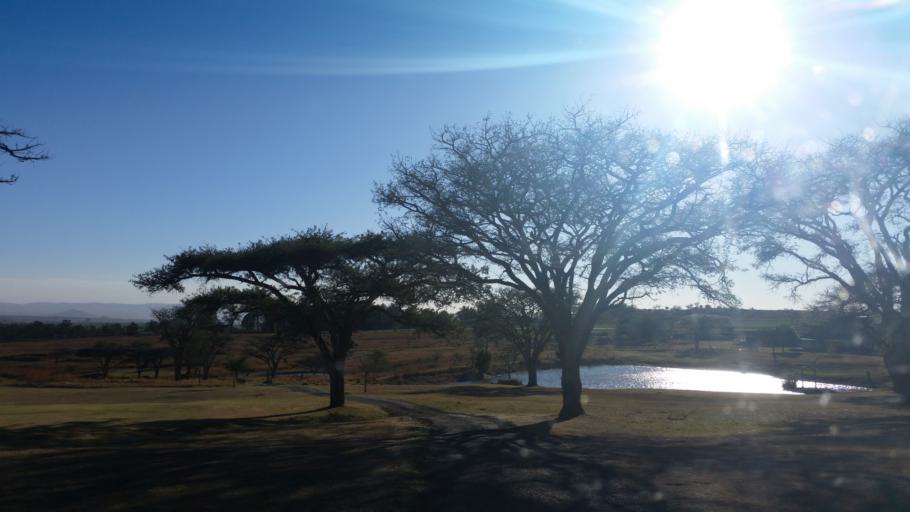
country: ZA
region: KwaZulu-Natal
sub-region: Amajuba District Municipality
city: Newcastle
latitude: -27.8040
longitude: 29.9528
